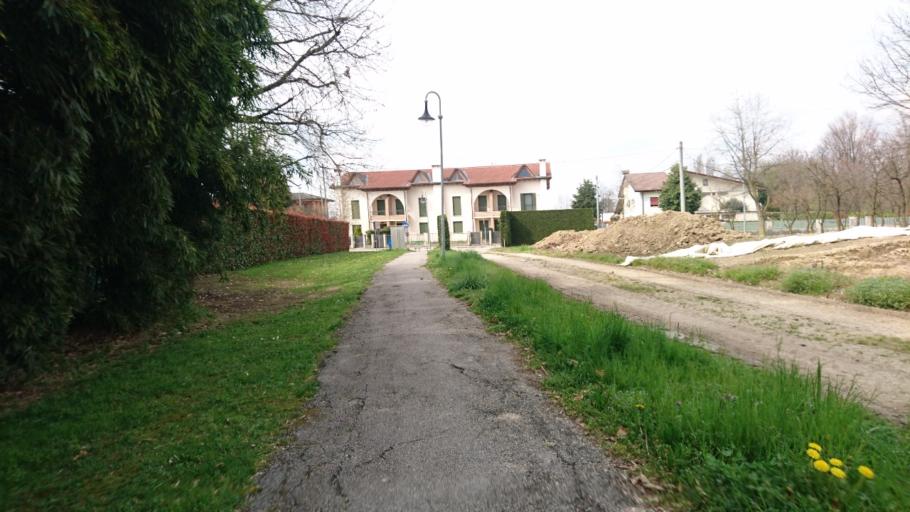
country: IT
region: Veneto
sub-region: Provincia di Padova
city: Villafranca Padovana
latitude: 45.4944
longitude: 11.8227
